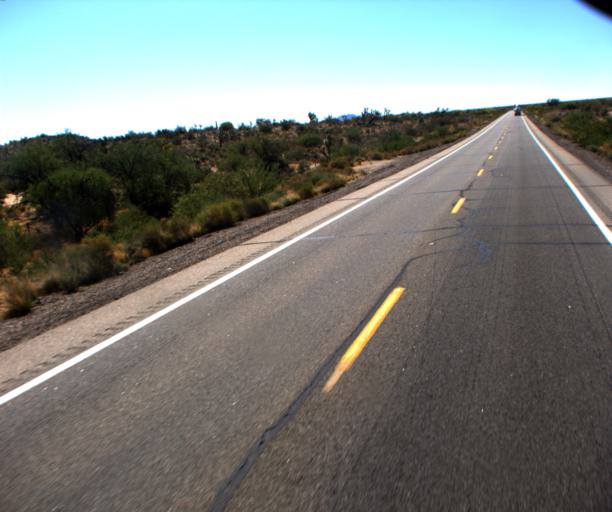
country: US
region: Arizona
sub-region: Yavapai County
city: Bagdad
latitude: 34.3282
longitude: -113.1411
